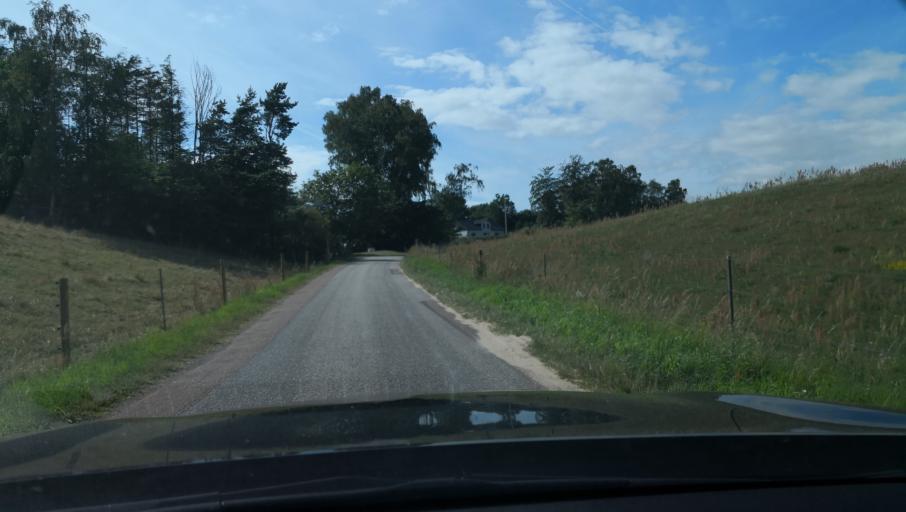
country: SE
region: Skane
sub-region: Ystads Kommun
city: Kopingebro
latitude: 55.3879
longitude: 14.1443
